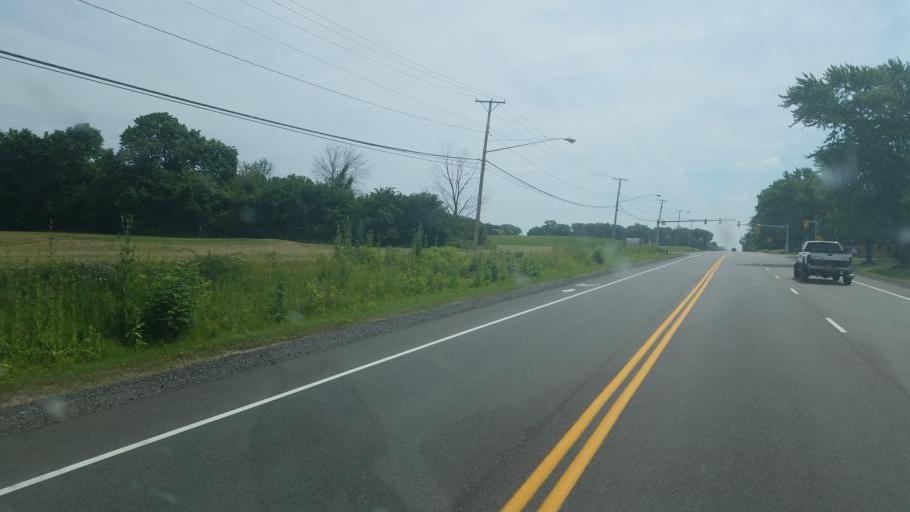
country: US
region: Ohio
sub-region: Summit County
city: Macedonia
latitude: 41.3114
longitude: -81.4838
